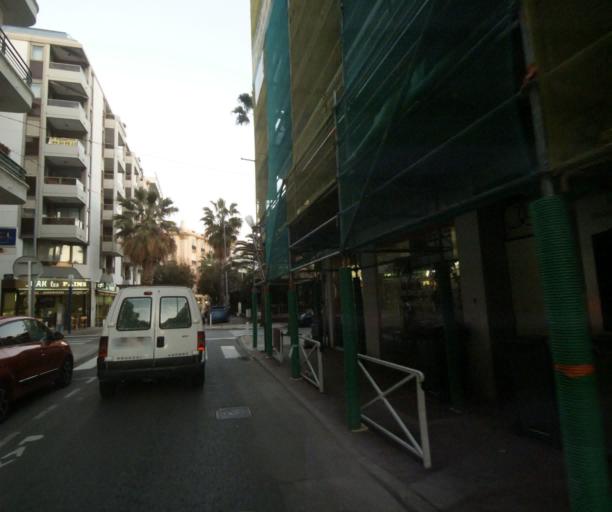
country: FR
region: Provence-Alpes-Cote d'Azur
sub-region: Departement des Alpes-Maritimes
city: Antibes
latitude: 43.5694
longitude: 7.1108
